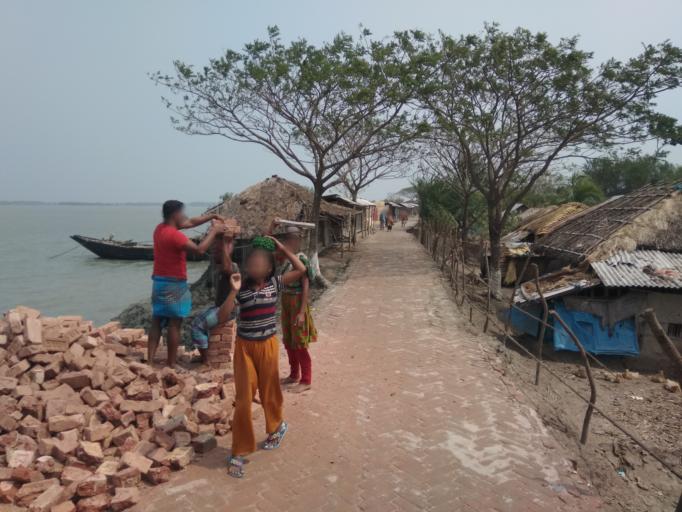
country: IN
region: West Bengal
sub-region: North 24 Parganas
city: Taki
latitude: 22.2809
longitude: 89.2913
